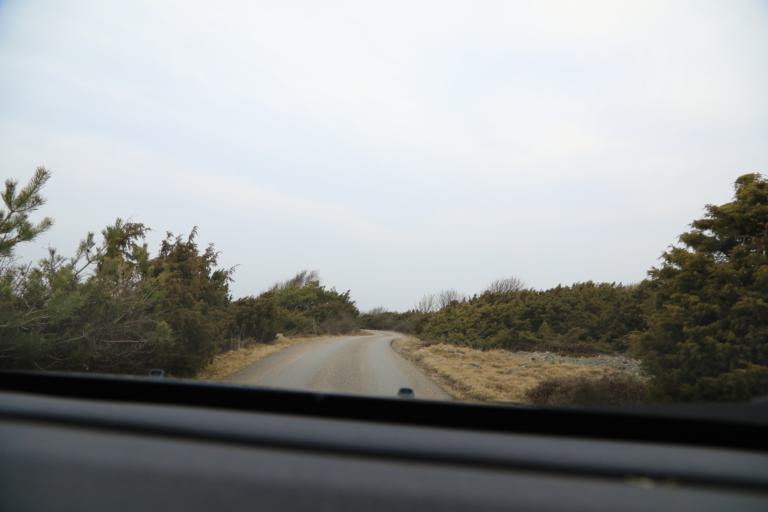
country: SE
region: Halland
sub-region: Kungsbacka Kommun
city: Frillesas
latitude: 57.2658
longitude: 12.1102
